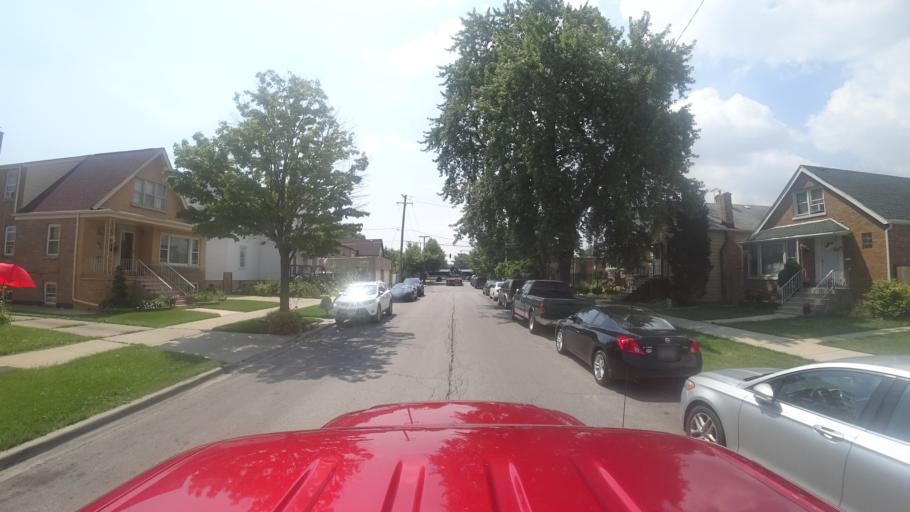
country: US
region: Illinois
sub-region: Cook County
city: Hometown
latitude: 41.7942
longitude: -87.7158
